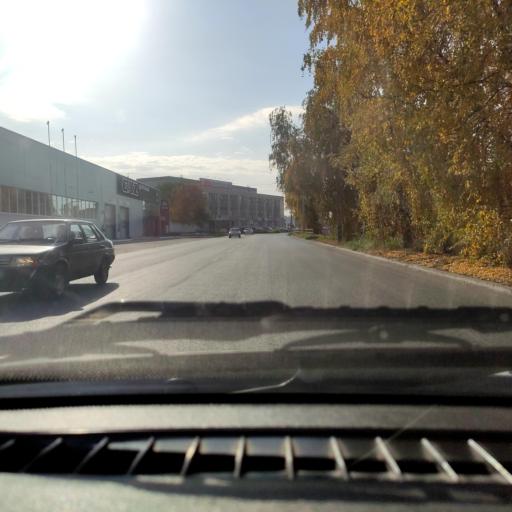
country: RU
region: Samara
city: Tol'yatti
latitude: 53.5307
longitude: 49.4307
